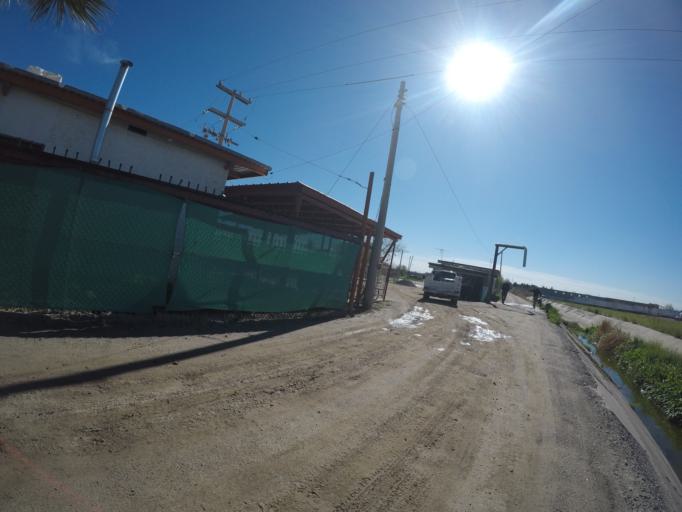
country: US
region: Texas
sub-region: El Paso County
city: Socorro
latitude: 31.6457
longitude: -106.3385
